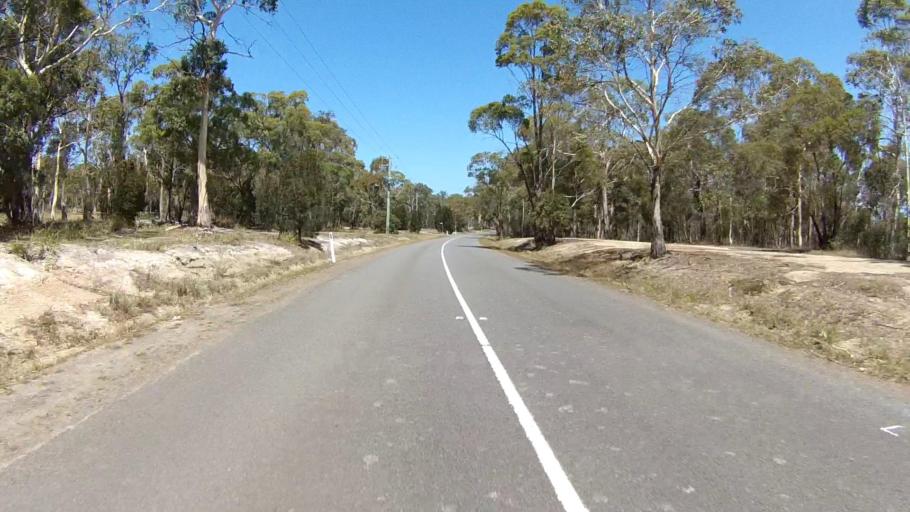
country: AU
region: Tasmania
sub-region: Clarence
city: Sandford
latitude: -42.9696
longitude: 147.4796
